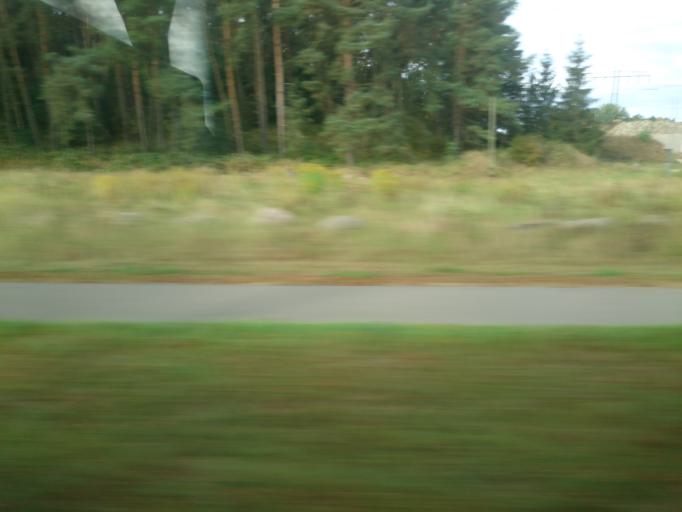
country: DE
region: Mecklenburg-Vorpommern
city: Jatznick
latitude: 53.5535
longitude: 13.9680
